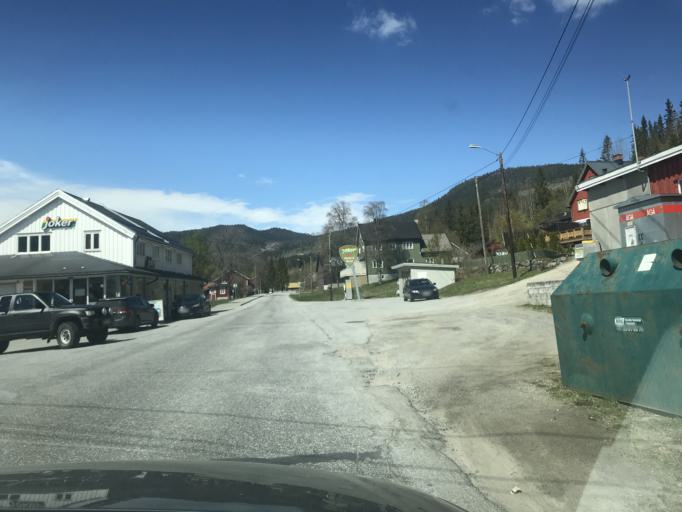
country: NO
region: Telemark
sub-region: Hjartdal
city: Sauland
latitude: 59.7508
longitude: 8.7989
